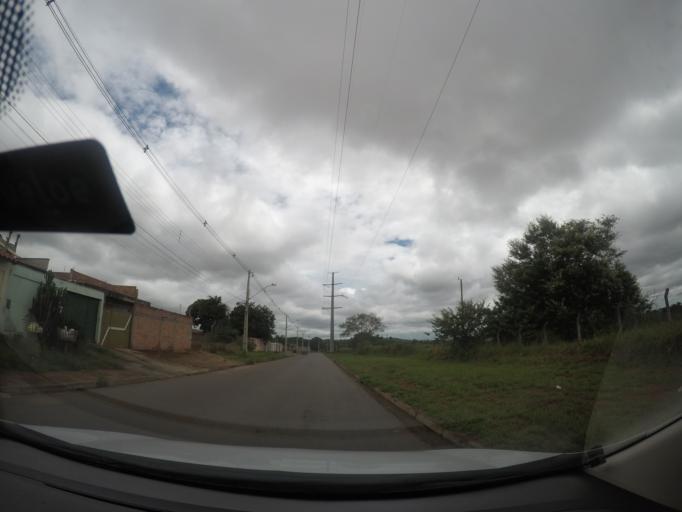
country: BR
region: Goias
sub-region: Goiania
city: Goiania
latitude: -16.7269
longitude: -49.3582
